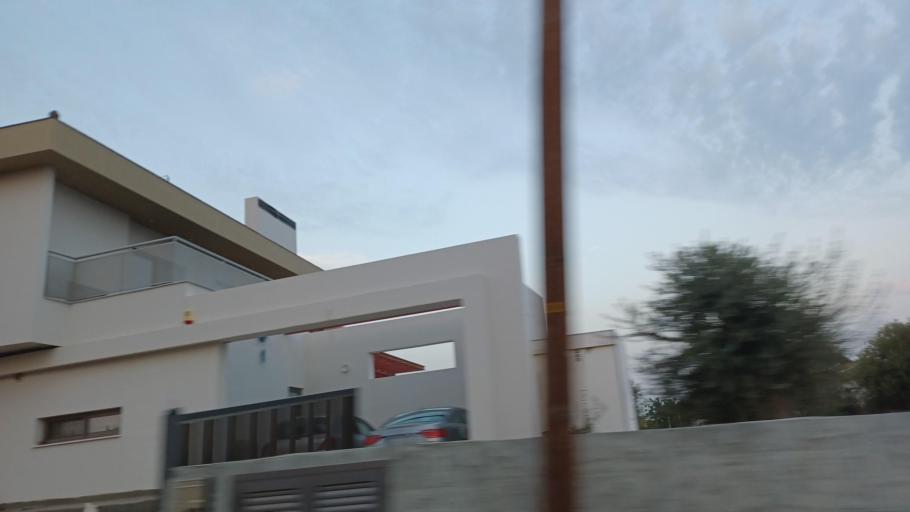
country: CY
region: Limassol
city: Ypsonas
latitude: 34.6899
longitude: 32.9670
